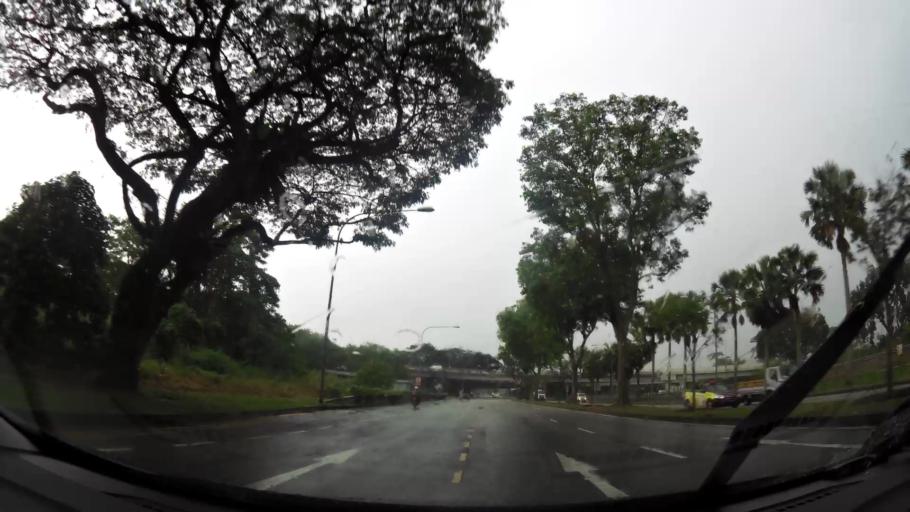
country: MY
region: Johor
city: Kampung Pasir Gudang Baru
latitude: 1.3931
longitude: 103.8356
